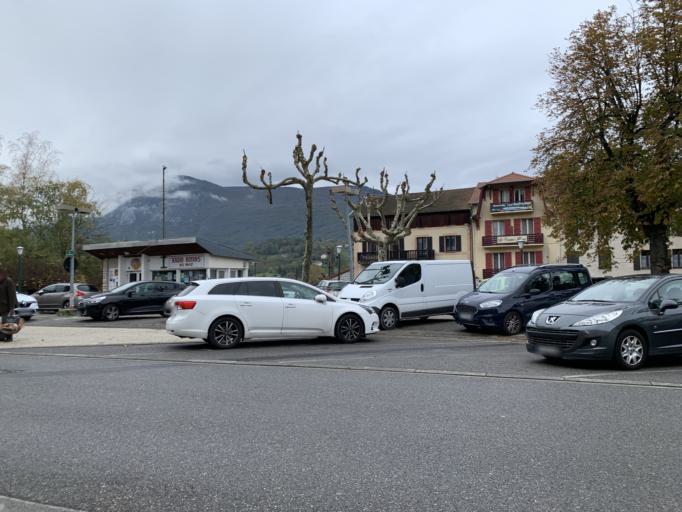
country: FR
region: Rhone-Alpes
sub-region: Departement de la Drome
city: Saint-Jean-en-Royans
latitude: 45.0189
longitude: 5.2928
